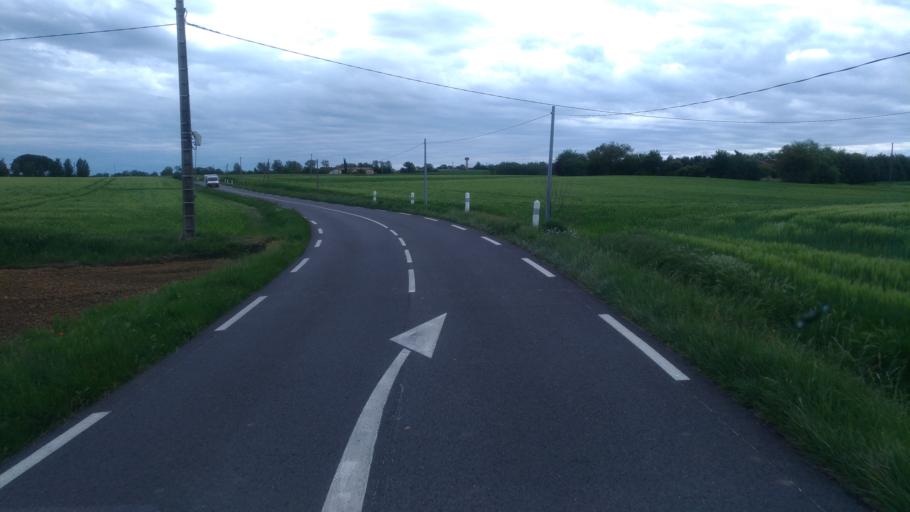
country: FR
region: Midi-Pyrenees
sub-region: Departement de la Haute-Garonne
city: Villefranche-de-Lauragais
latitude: 43.4264
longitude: 1.7627
